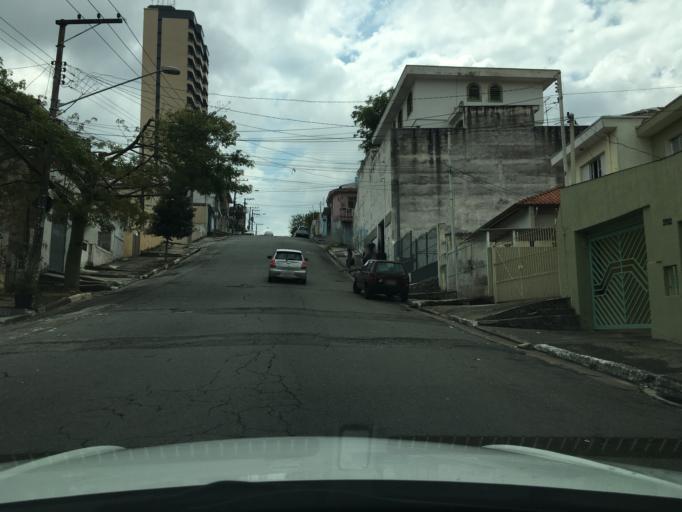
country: BR
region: Sao Paulo
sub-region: Sao Paulo
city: Sao Paulo
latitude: -23.4956
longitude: -46.6497
